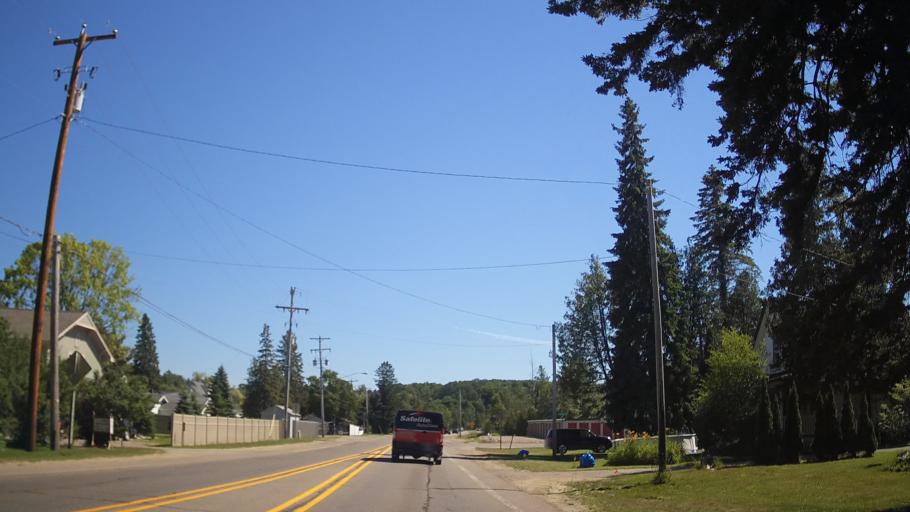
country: US
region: Michigan
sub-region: Emmet County
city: Petoskey
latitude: 45.4160
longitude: -84.8654
